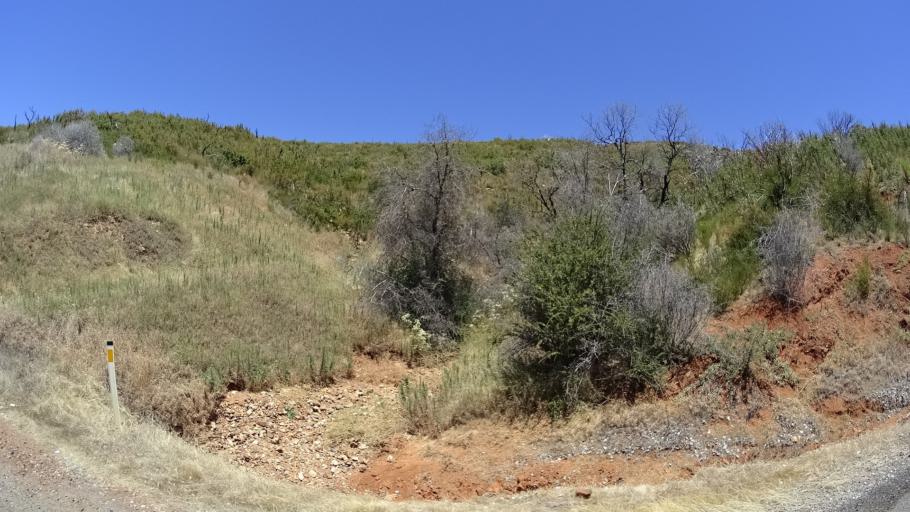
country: US
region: California
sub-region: Calaveras County
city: Mountain Ranch
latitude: 38.2897
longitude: -120.6107
